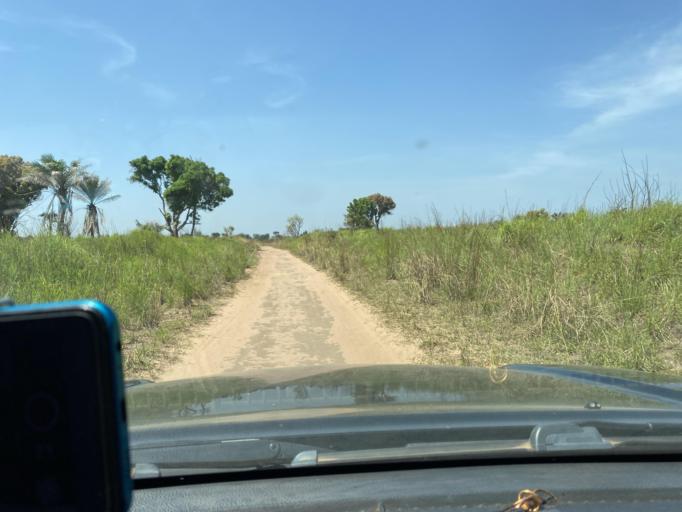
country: CD
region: Kasai-Oriental
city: Kabinda
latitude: -5.8822
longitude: 24.8712
